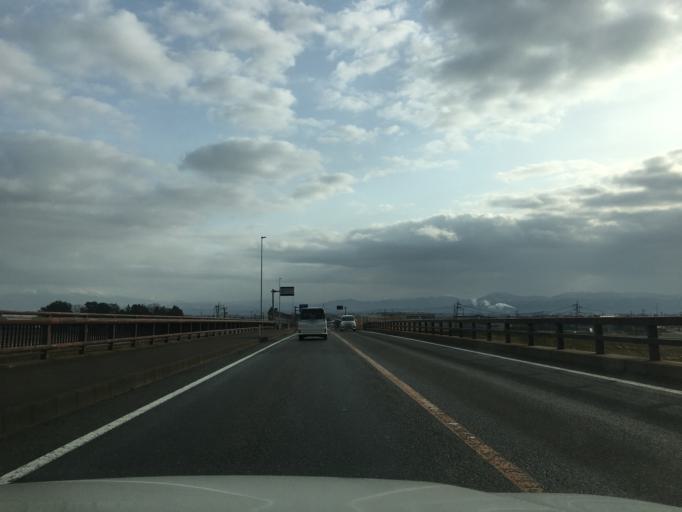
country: JP
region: Yamagata
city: Sakata
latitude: 38.8262
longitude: 139.8407
